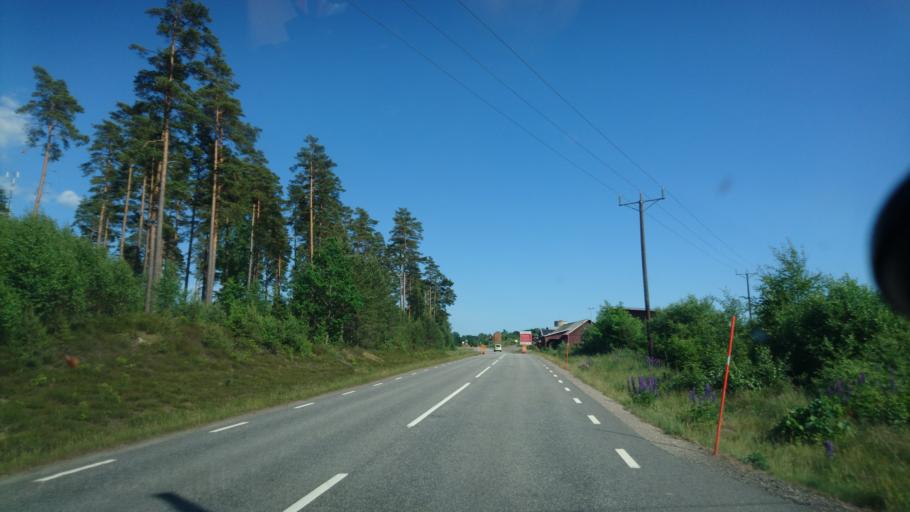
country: SE
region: Skane
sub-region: Osby Kommun
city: Lonsboda
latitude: 56.4108
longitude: 14.3064
